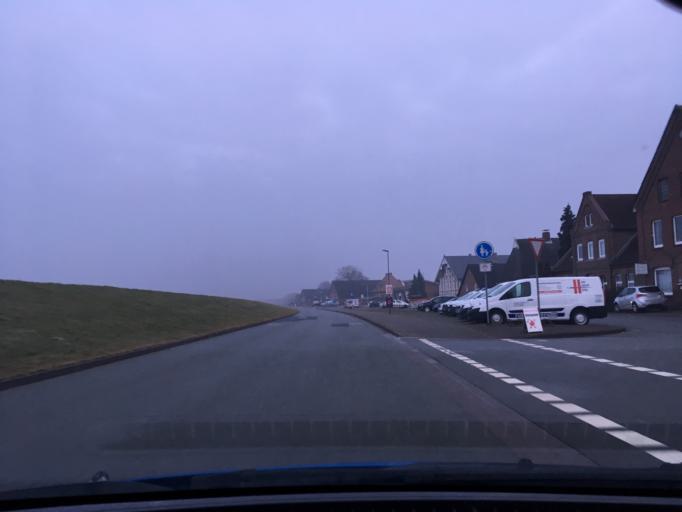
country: DE
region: Lower Saxony
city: Stelle
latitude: 53.4002
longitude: 10.1587
